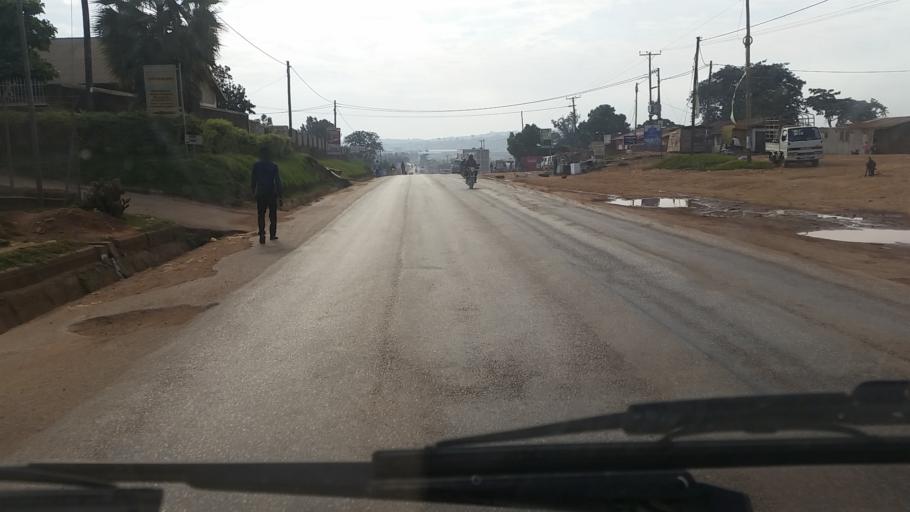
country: UG
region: Central Region
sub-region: Wakiso District
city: Bweyogerere
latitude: 0.3537
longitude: 32.6715
